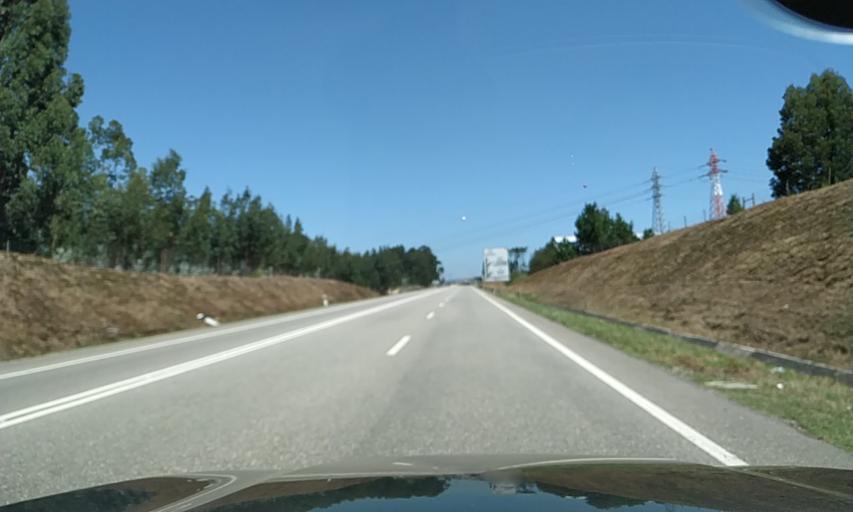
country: PT
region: Aveiro
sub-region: Agueda
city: Agueda
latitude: 40.5859
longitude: -8.4717
